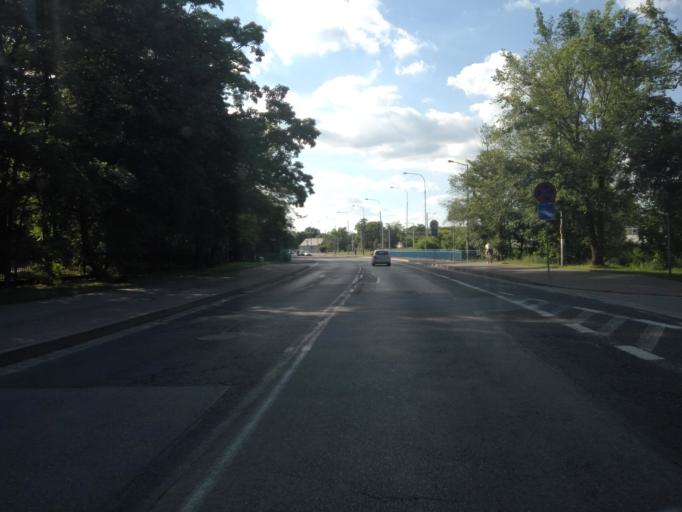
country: PL
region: Lower Silesian Voivodeship
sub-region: Powiat wroclawski
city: Wroclaw
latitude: 51.1417
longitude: 16.9568
